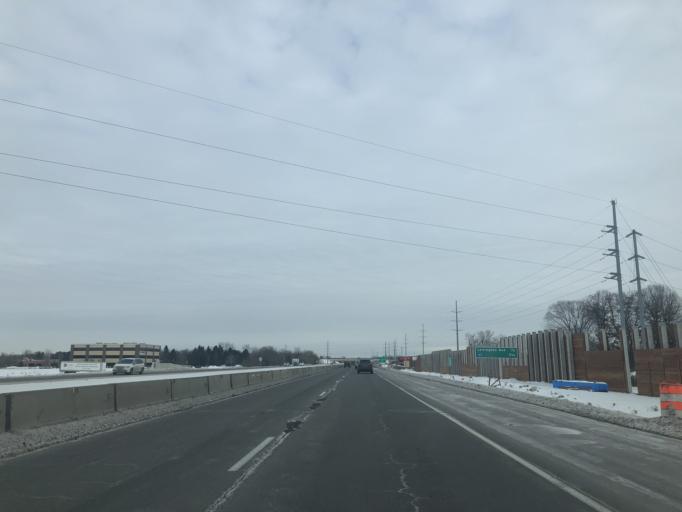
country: US
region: Minnesota
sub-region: Anoka County
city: Lexington
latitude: 45.1529
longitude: -93.1728
